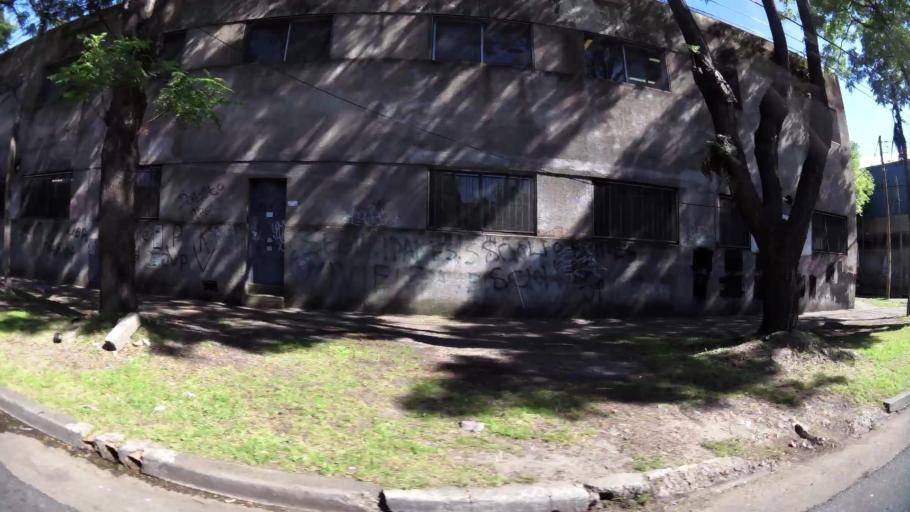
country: AR
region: Buenos Aires
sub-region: Partido de General San Martin
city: General San Martin
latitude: -34.5377
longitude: -58.5196
